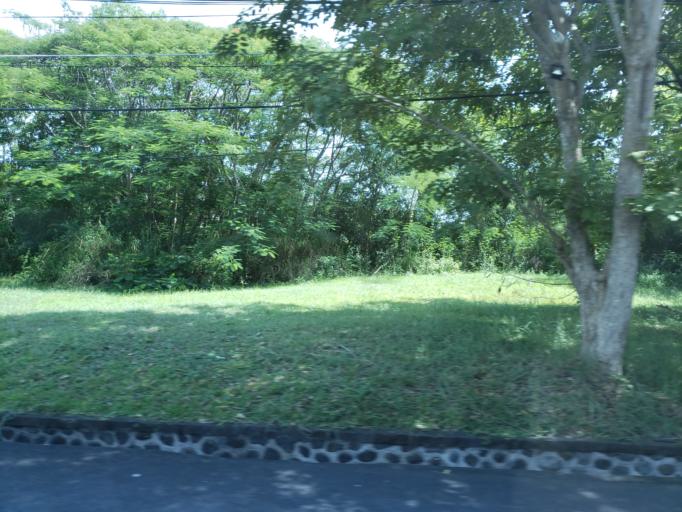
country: ID
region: Bali
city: Jimbaran
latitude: -8.7842
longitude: 115.1600
